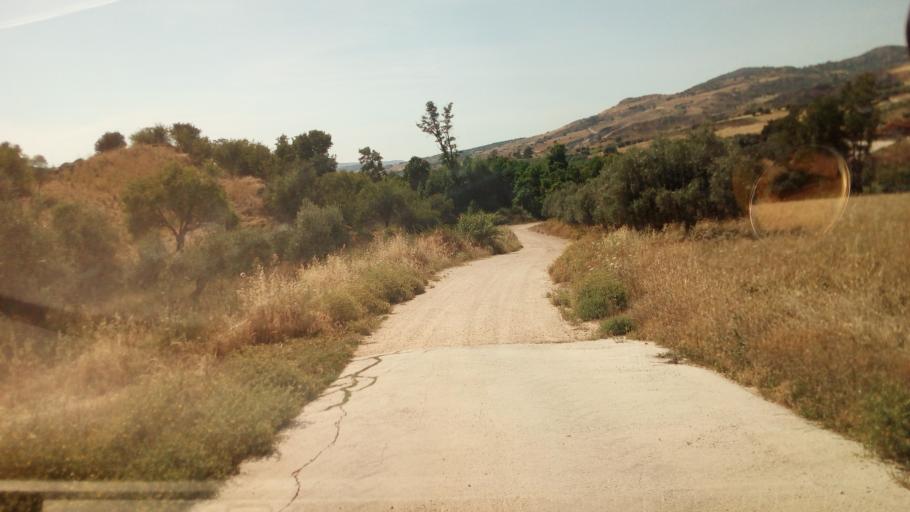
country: CY
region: Pafos
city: Polis
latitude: 34.9516
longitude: 32.5216
